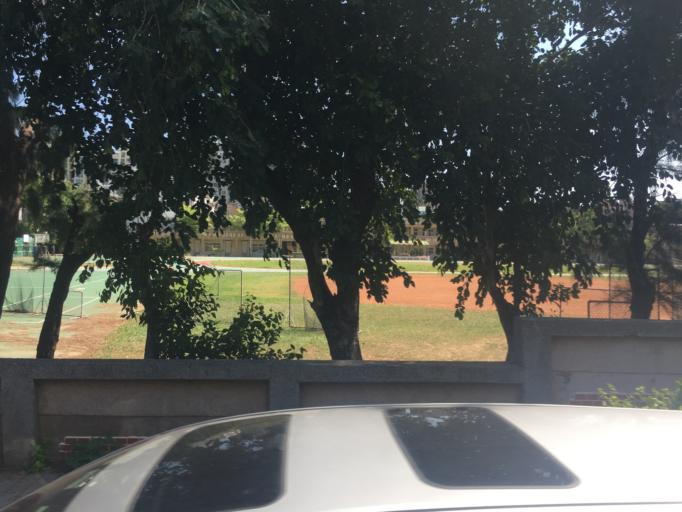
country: TW
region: Taiwan
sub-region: Hsinchu
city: Hsinchu
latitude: 24.7983
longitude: 120.9841
